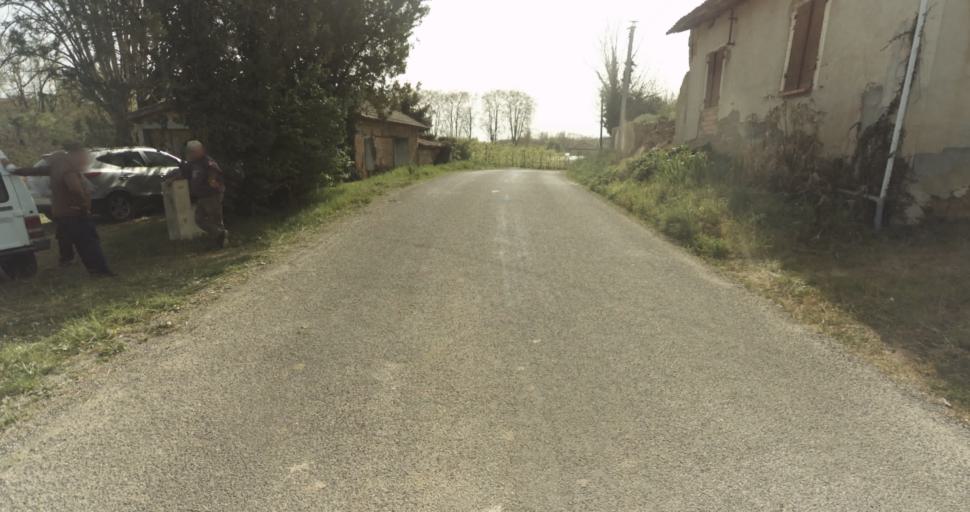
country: FR
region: Midi-Pyrenees
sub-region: Departement du Tarn-et-Garonne
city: Lafrancaise
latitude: 44.1506
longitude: 1.1858
